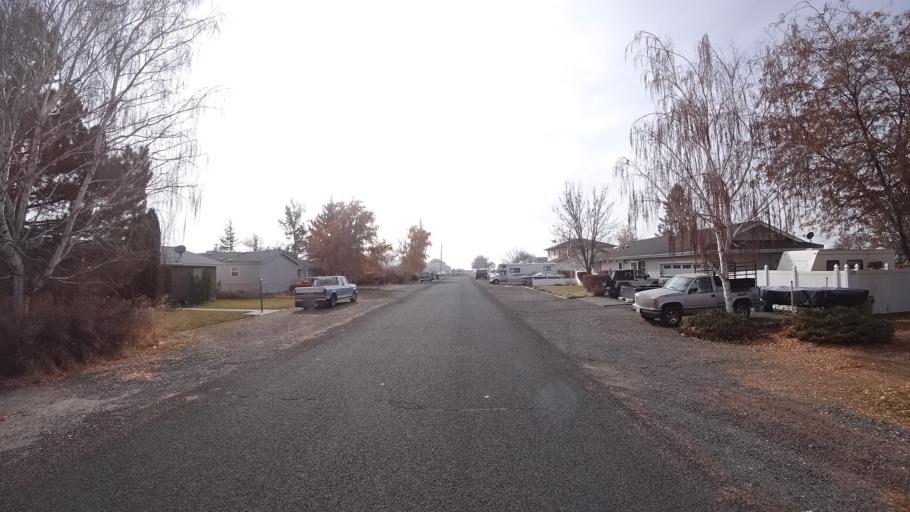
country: US
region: California
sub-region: Siskiyou County
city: Tulelake
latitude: 41.9522
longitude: -121.4810
